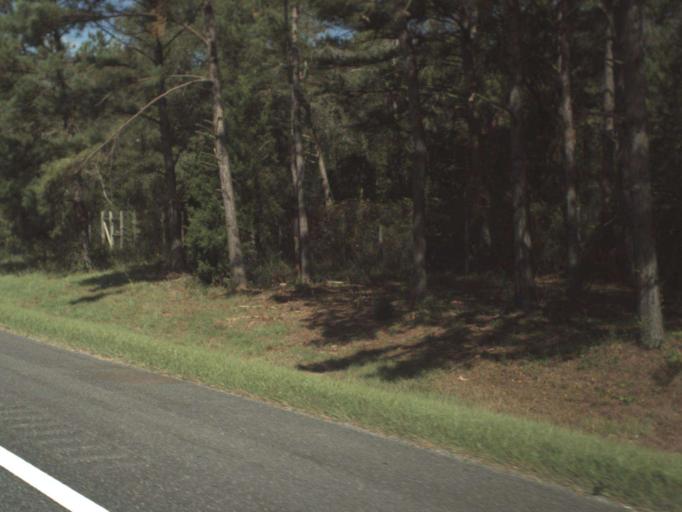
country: US
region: Florida
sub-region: Jackson County
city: Marianna
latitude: 30.7451
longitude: -85.2552
